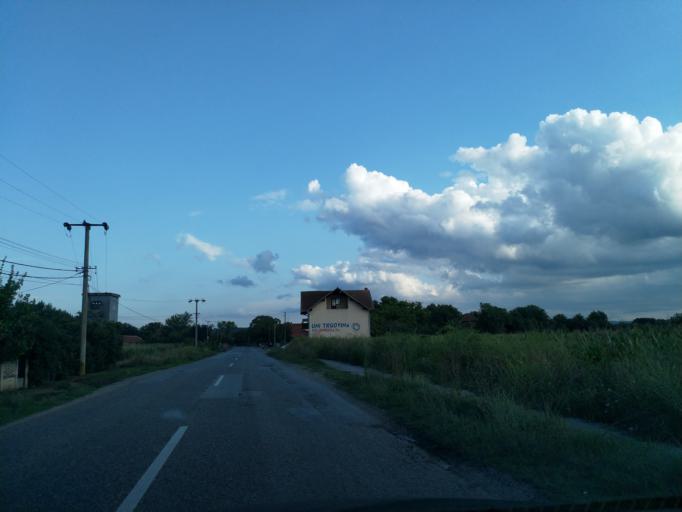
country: RS
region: Central Serbia
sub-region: Rasinski Okrug
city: Cicevac
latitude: 43.7589
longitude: 21.4329
